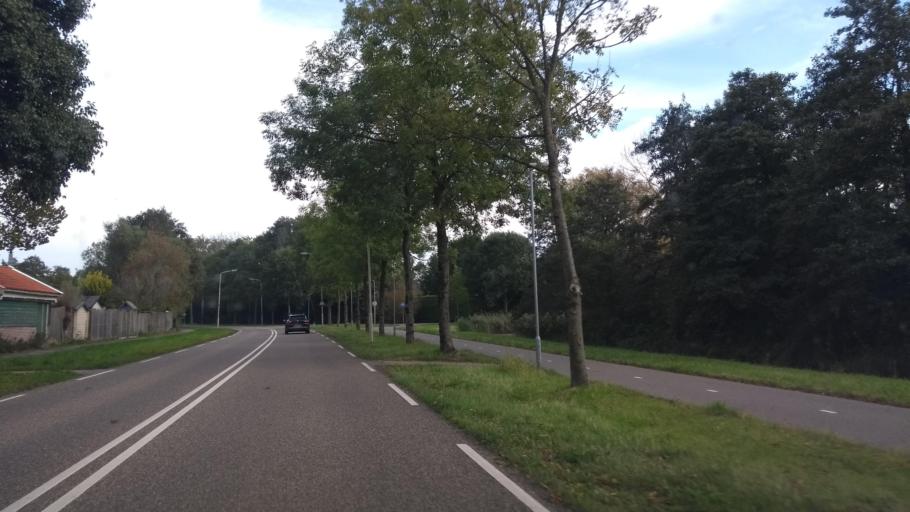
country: NL
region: North Holland
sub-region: Gemeente Langedijk
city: Broek op Langedijk
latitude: 52.6915
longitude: 4.8130
